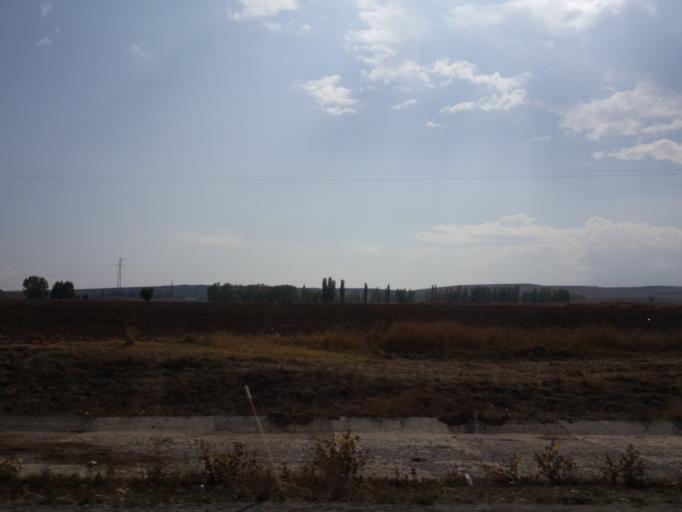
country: TR
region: Corum
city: Alaca
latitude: 40.1430
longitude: 34.8285
